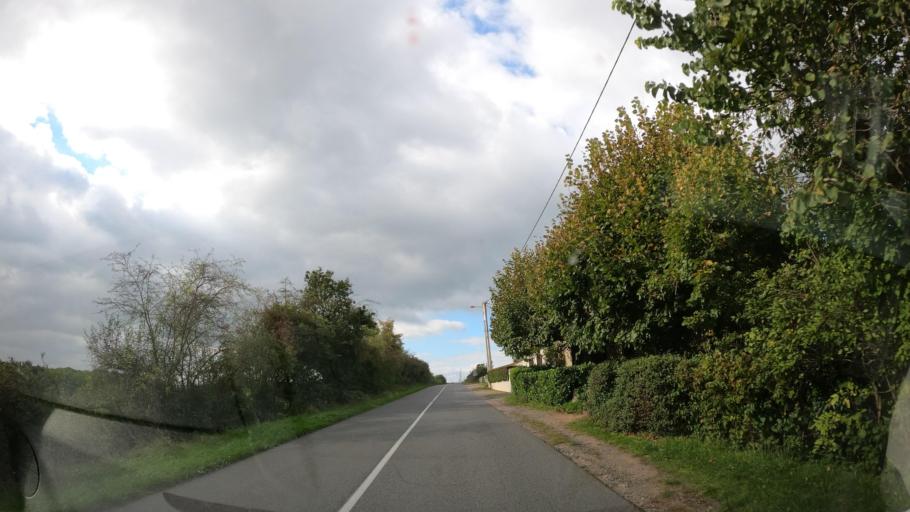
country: FR
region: Auvergne
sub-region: Departement de l'Allier
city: Lapalisse
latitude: 46.3770
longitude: 3.5993
